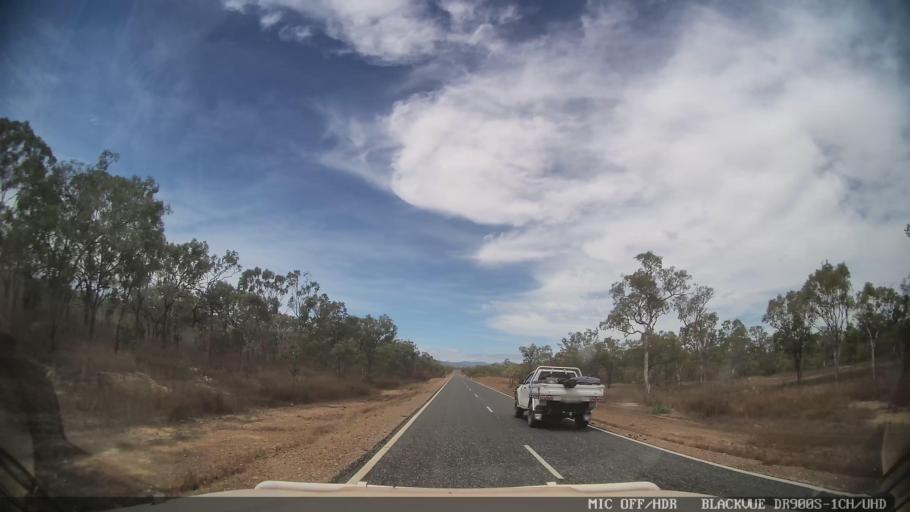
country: AU
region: Queensland
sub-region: Cairns
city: Port Douglas
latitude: -16.5102
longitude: 145.0548
